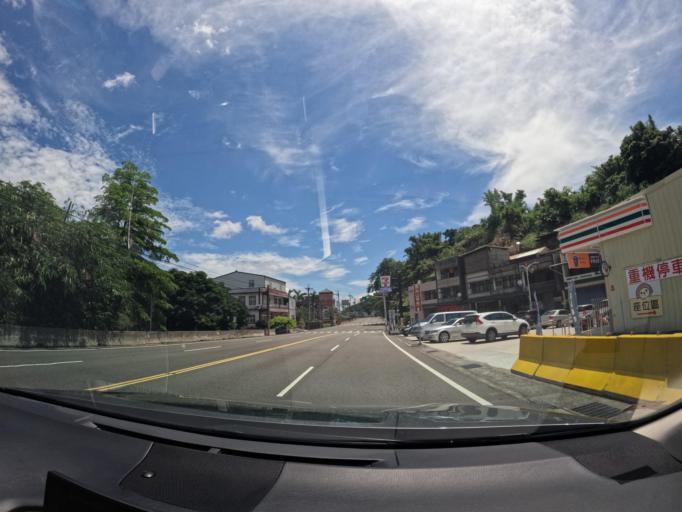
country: TW
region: Taiwan
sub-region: Miaoli
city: Miaoli
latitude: 24.5437
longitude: 120.9226
